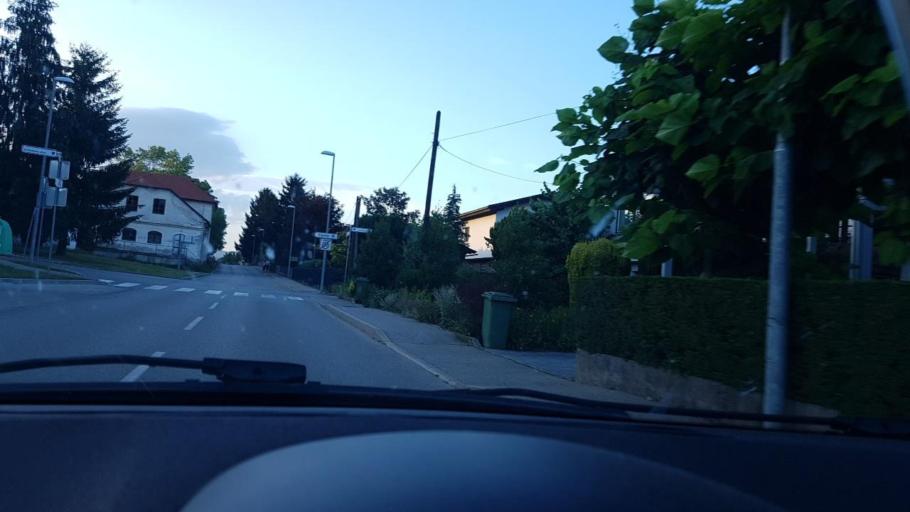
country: SI
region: Brezice
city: Brezice
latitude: 45.9048
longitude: 15.5940
